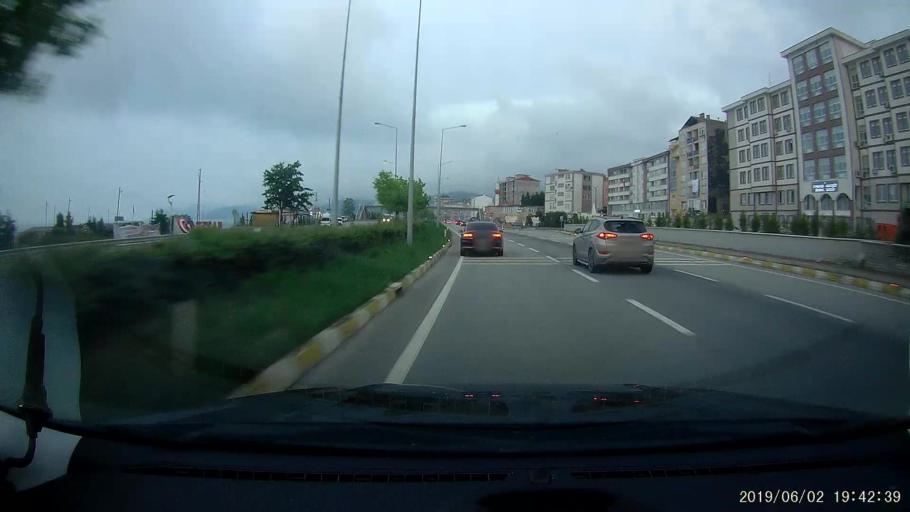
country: TR
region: Giresun
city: Kesap
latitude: 40.9172
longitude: 38.5099
